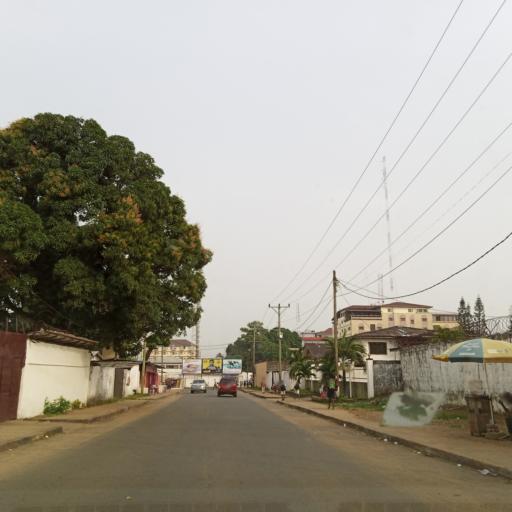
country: LR
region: Montserrado
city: Monrovia
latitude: 6.2942
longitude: -10.7827
